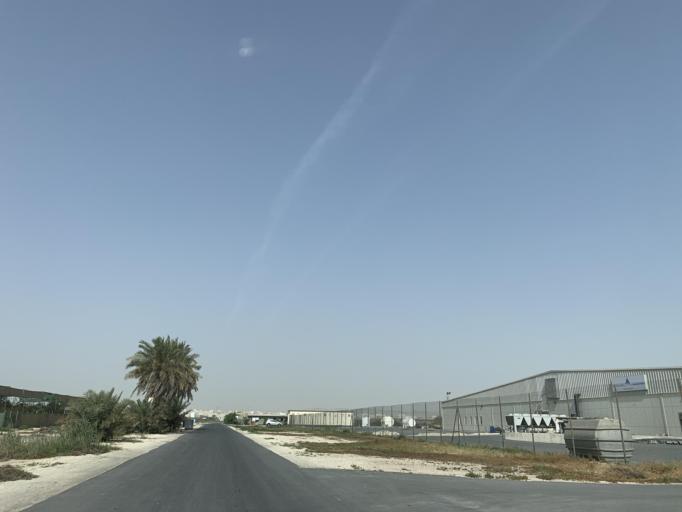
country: BH
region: Northern
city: Madinat `Isa
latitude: 26.1724
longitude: 50.5346
